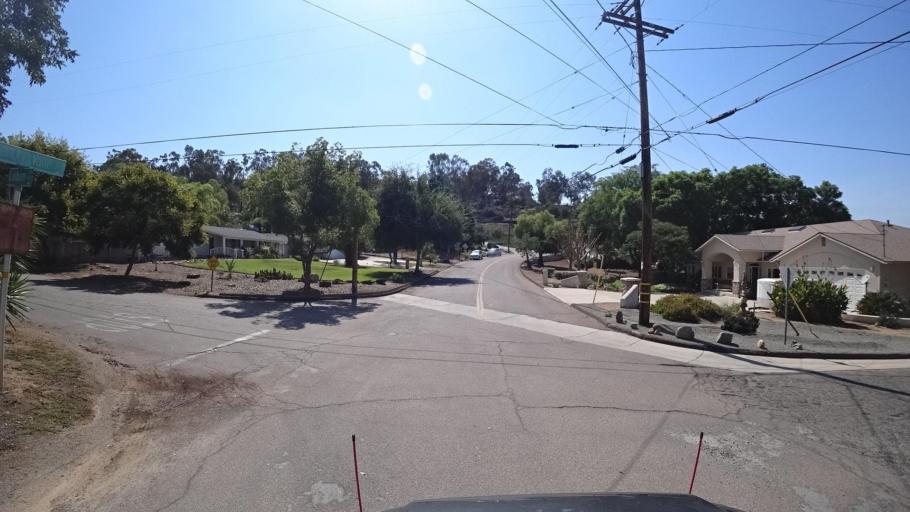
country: US
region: California
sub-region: San Diego County
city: Granite Hills
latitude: 32.7792
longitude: -116.9187
